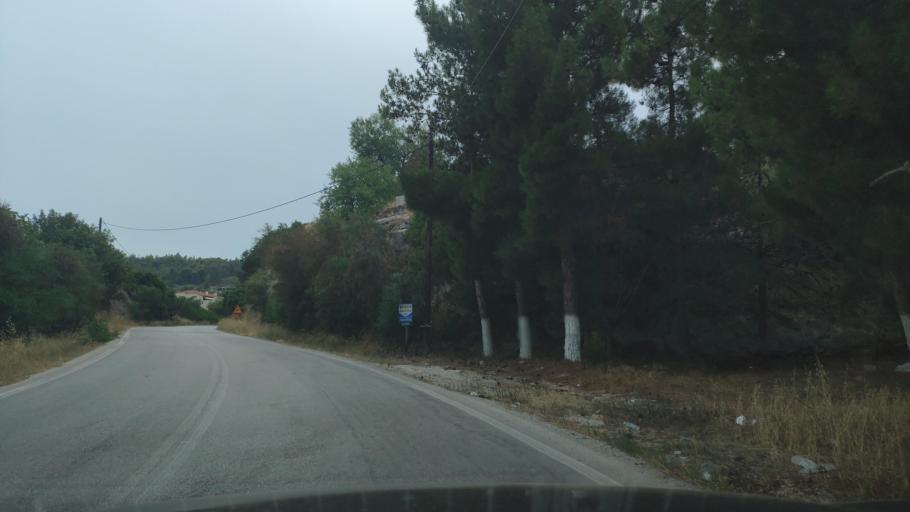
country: GR
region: Peloponnese
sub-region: Nomos Argolidos
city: Kranidi
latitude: 37.3824
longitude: 23.1536
